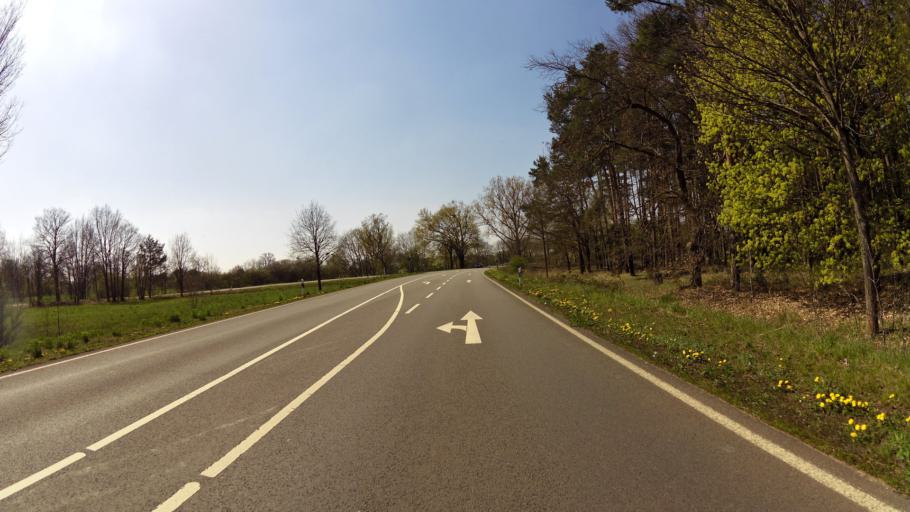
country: DE
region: Saxony-Anhalt
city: Mieste
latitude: 52.4681
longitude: 11.1187
